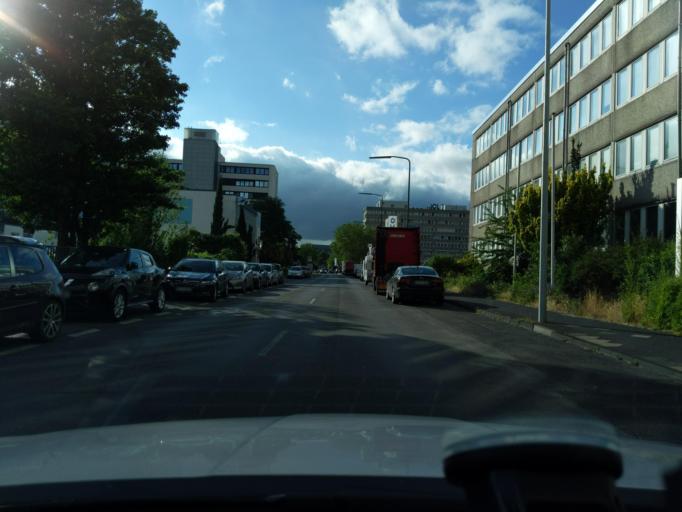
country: DE
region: North Rhine-Westphalia
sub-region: Regierungsbezirk Dusseldorf
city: Dusseldorf
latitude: 51.2569
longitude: 6.8008
